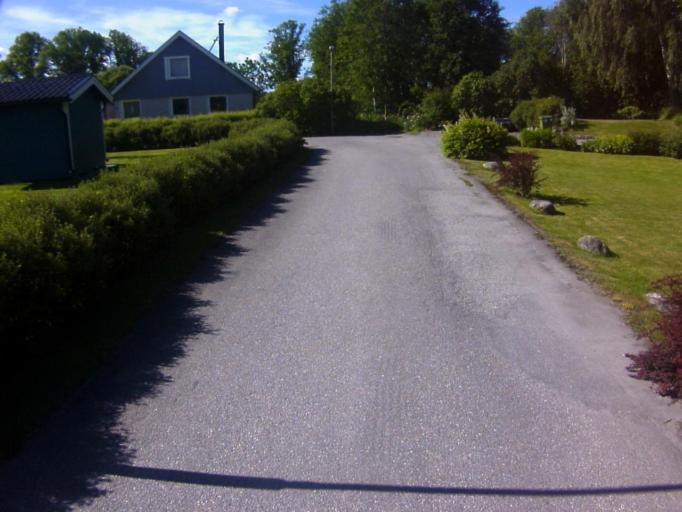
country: SE
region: Soedermanland
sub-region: Eskilstuna Kommun
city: Skogstorp
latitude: 59.3166
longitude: 16.4615
